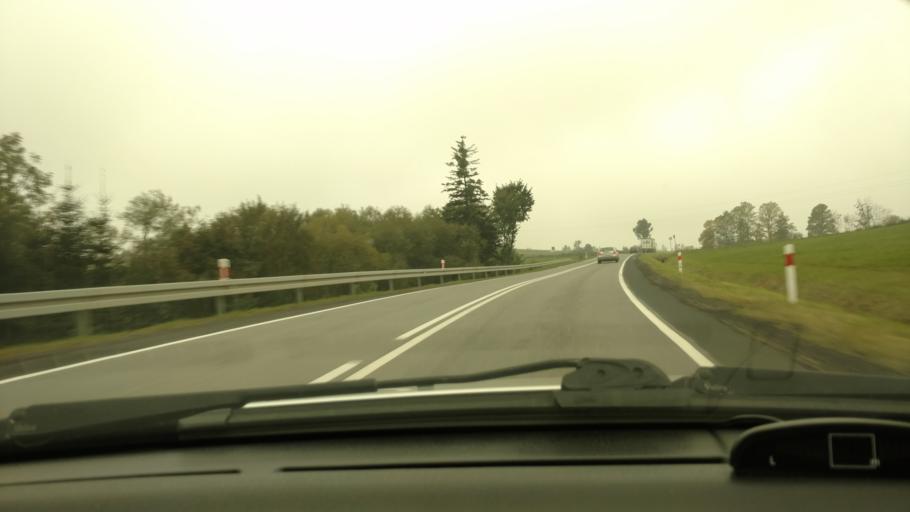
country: PL
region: Lesser Poland Voivodeship
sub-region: Powiat nowosadecki
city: Grybow
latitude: 49.6128
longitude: 20.8824
